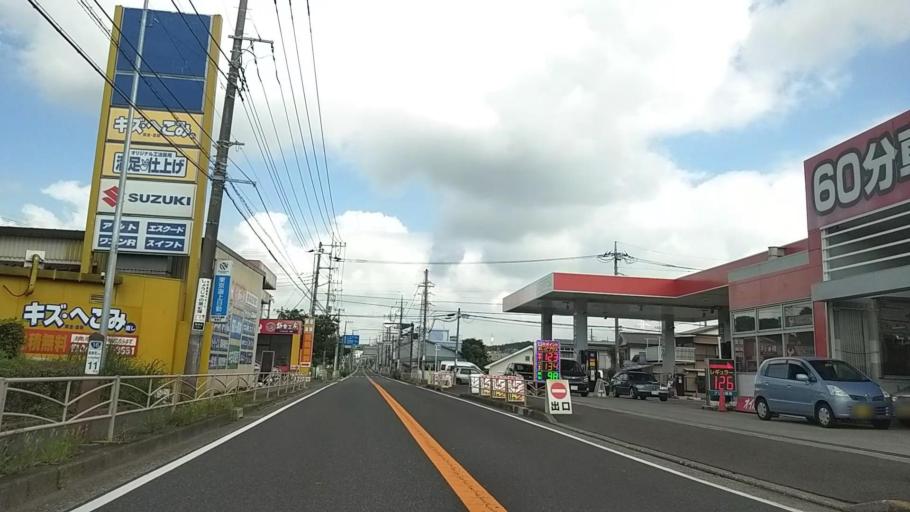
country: JP
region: Kanagawa
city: Minami-rinkan
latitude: 35.4866
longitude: 139.5206
